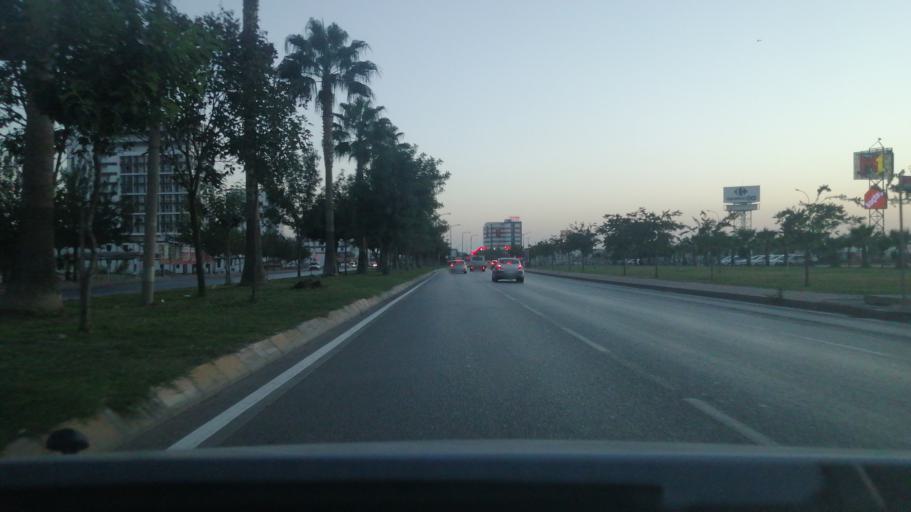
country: TR
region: Adana
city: Seyhan
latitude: 37.0181
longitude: 35.2518
